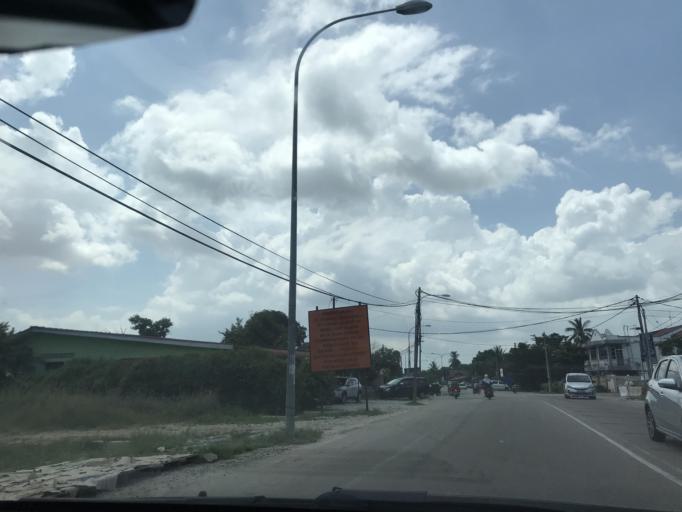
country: MY
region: Kelantan
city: Kota Bharu
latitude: 6.1183
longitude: 102.1938
